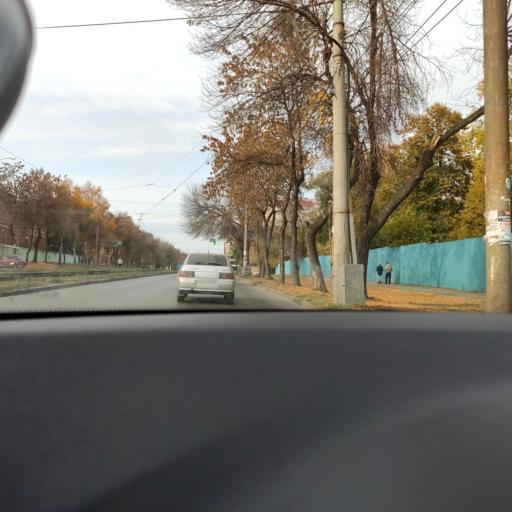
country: RU
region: Samara
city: Samara
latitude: 53.2259
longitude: 50.2329
